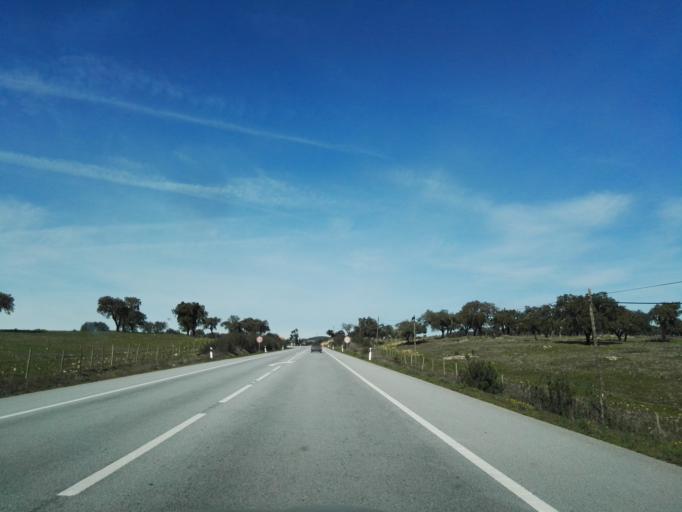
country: PT
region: Portalegre
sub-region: Portalegre
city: Urra
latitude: 39.2016
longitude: -7.3658
